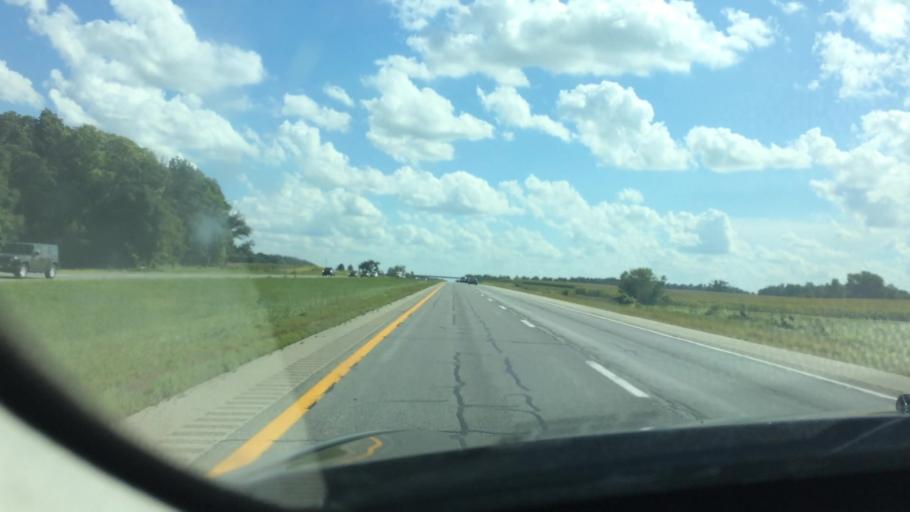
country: US
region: Ohio
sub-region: Shelby County
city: Botkins
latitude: 40.4910
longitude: -84.1692
